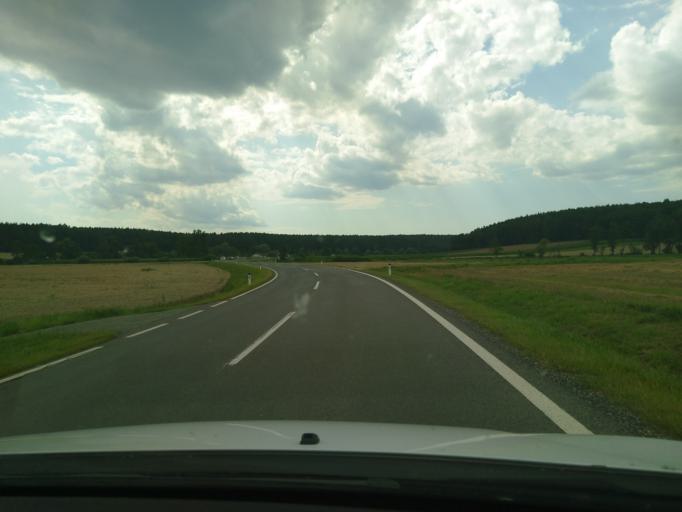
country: AT
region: Burgenland
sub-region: Politischer Bezirk Oberwart
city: Oberschutzen
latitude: 47.3517
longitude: 16.1853
